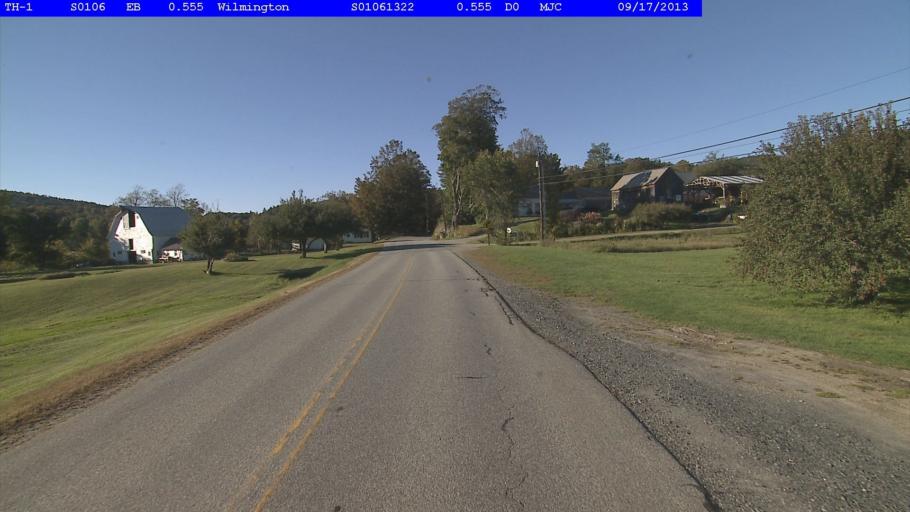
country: US
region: Vermont
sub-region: Windham County
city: Dover
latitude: 42.9201
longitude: -72.8361
